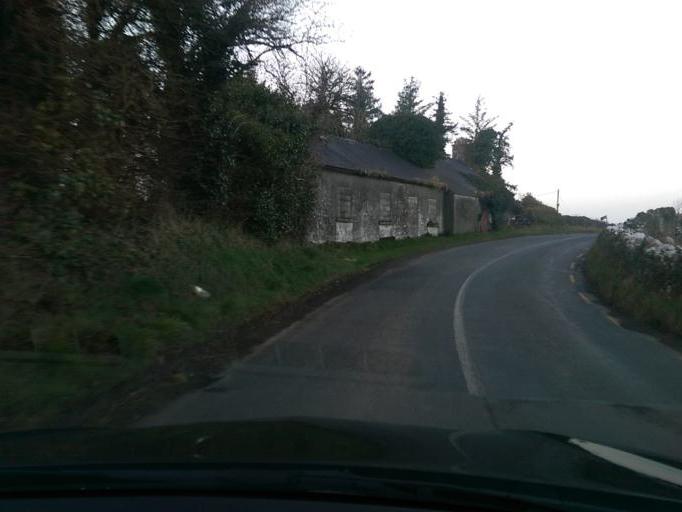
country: IE
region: Connaught
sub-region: County Galway
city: Athenry
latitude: 53.2370
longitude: -8.6628
